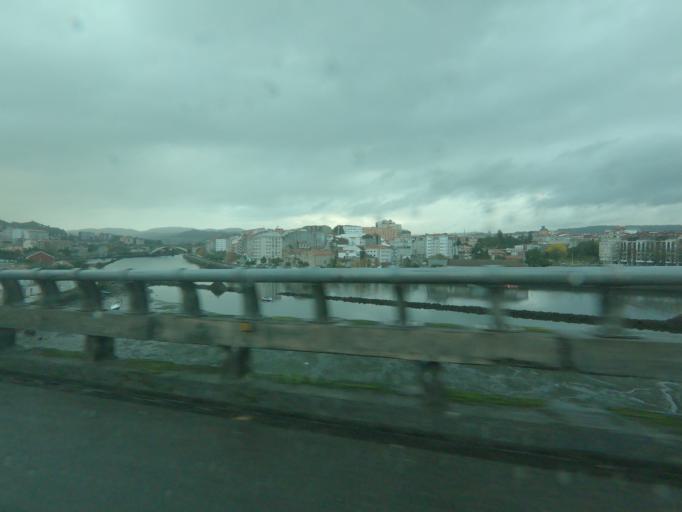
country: ES
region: Galicia
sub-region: Provincia de Pontevedra
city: Poio
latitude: 42.4279
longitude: -8.6557
